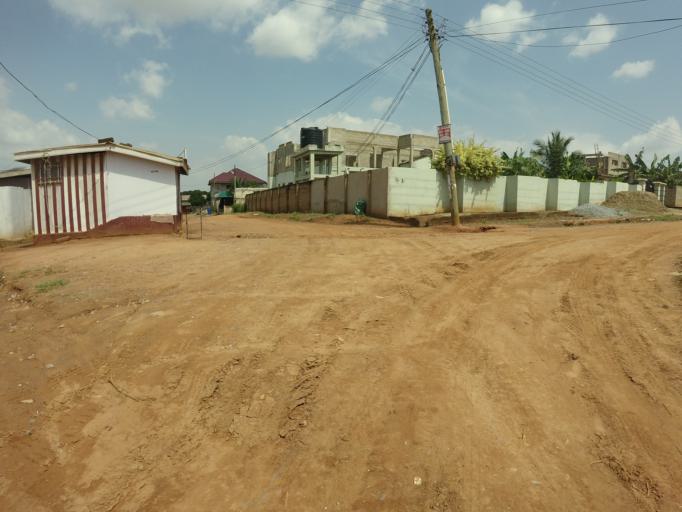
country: GH
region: Greater Accra
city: Gbawe
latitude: 5.6180
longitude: -0.3124
